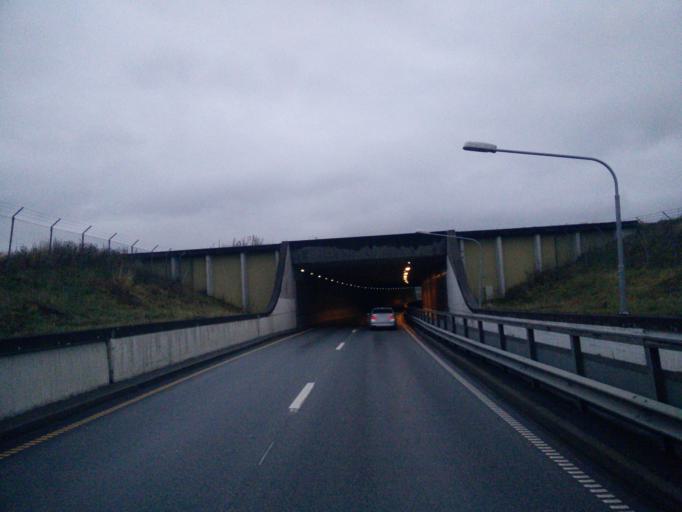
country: NO
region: Nord-Trondelag
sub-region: Stjordal
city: Stjordal
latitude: 63.4565
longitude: 10.9102
